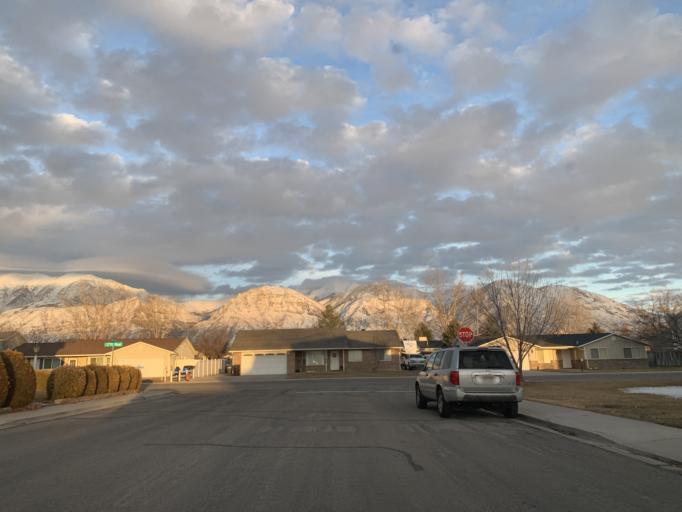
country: US
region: Utah
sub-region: Utah County
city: Provo
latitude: 40.2455
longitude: -111.7084
